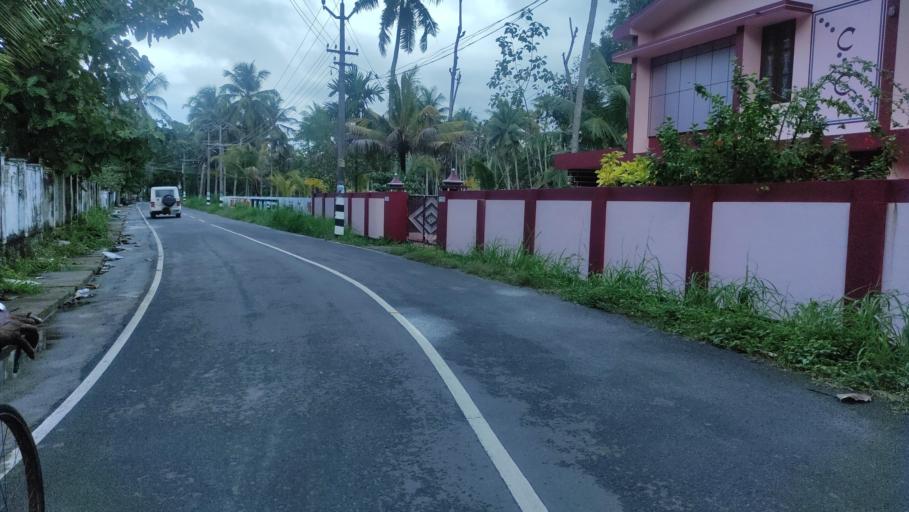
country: IN
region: Kerala
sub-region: Alappuzha
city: Kayankulam
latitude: 9.1956
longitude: 76.5038
